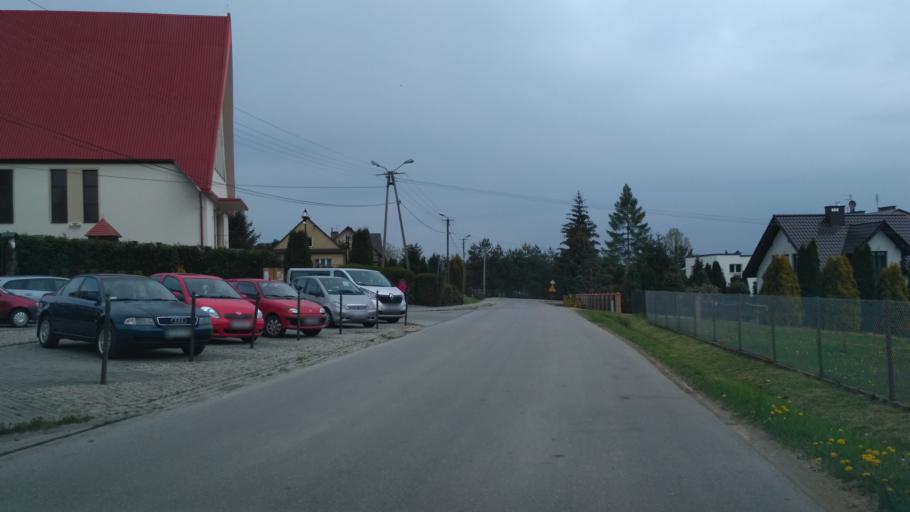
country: PL
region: Lesser Poland Voivodeship
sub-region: Powiat tarnowski
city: Tarnowiec
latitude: 49.9469
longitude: 21.0298
